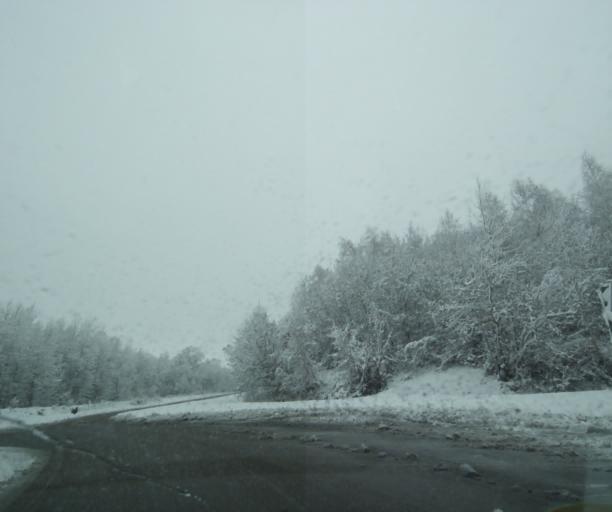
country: FR
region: Champagne-Ardenne
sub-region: Departement de la Haute-Marne
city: Saint-Dizier
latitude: 48.6056
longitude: 4.9100
